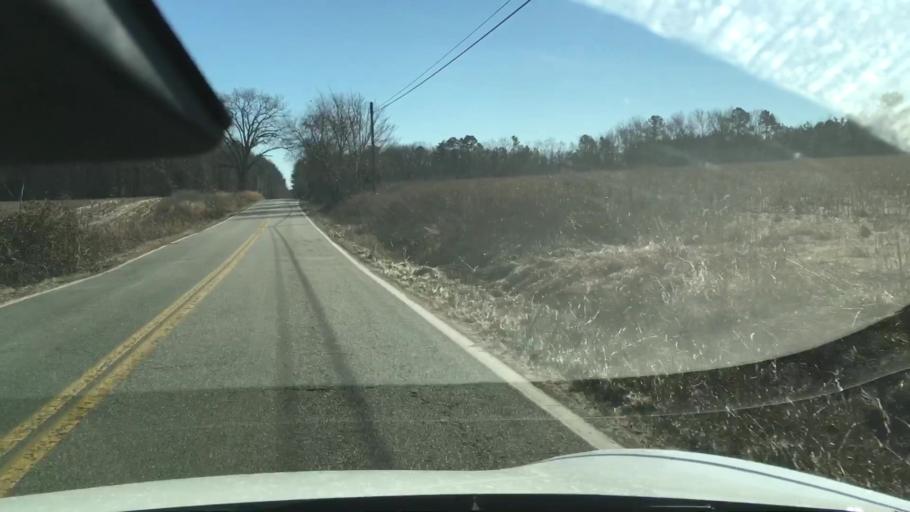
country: US
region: Virginia
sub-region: Henrico County
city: Short Pump
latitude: 37.5768
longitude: -77.7237
